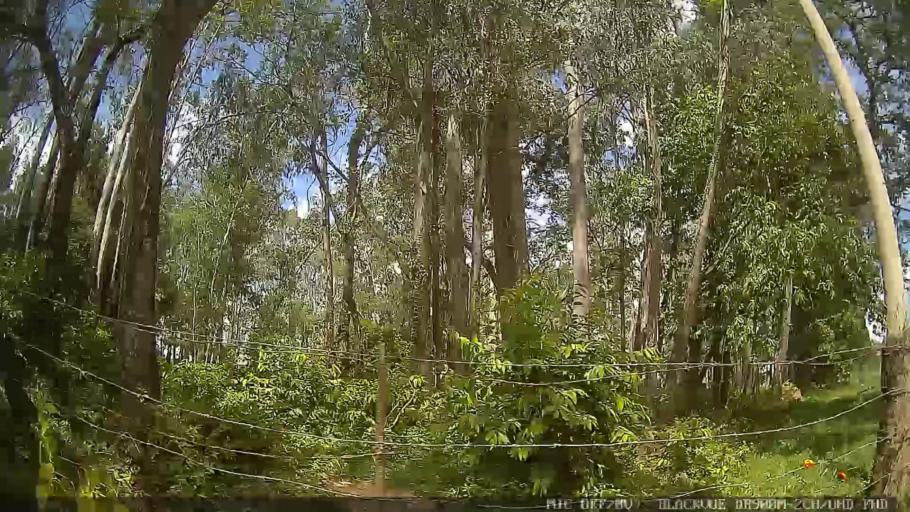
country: BR
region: Sao Paulo
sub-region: Conchas
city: Conchas
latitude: -23.0418
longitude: -47.9944
